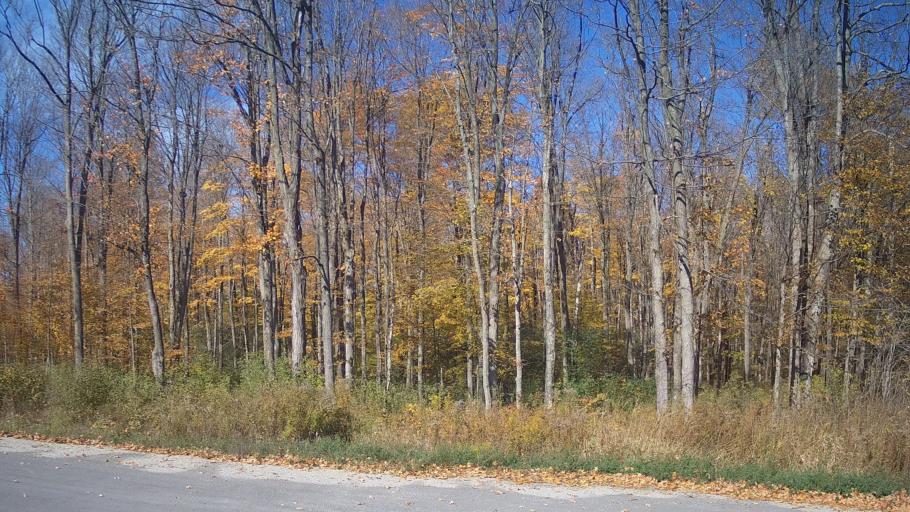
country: CA
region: Ontario
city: Perth
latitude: 44.8839
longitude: -76.2925
